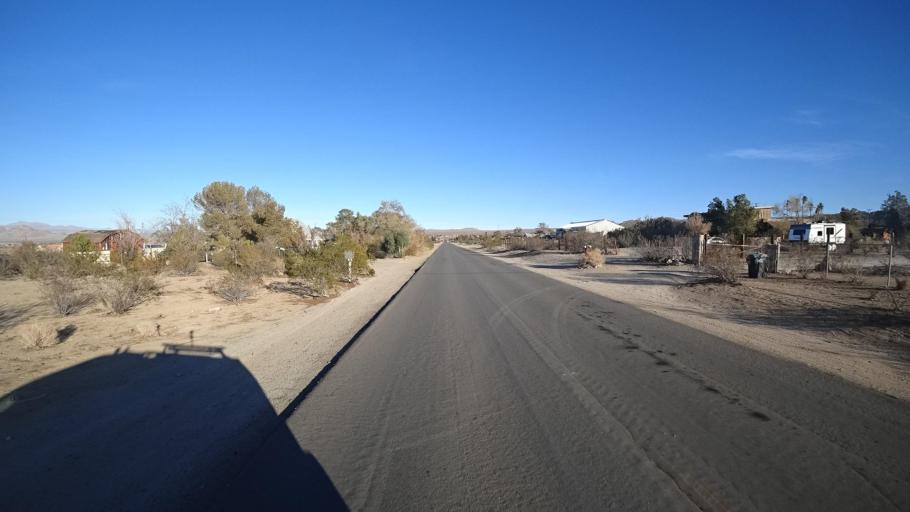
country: US
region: California
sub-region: Kern County
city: Ridgecrest
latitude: 35.5861
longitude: -117.6643
